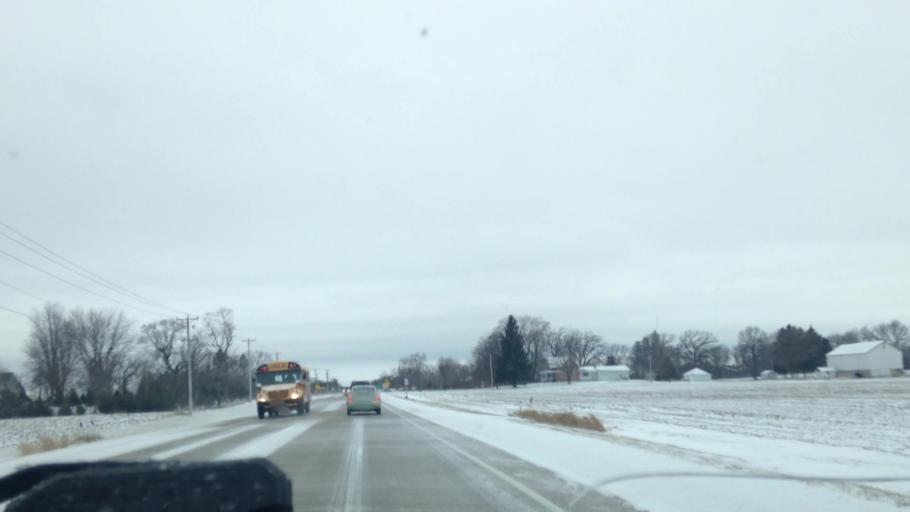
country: US
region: Wisconsin
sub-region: Dodge County
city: Juneau
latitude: 43.4448
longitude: -88.6902
